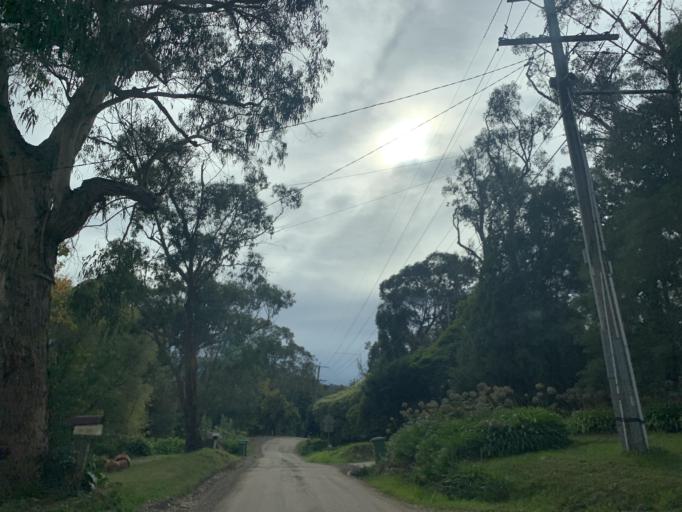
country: AU
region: Victoria
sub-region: Yarra Ranges
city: Belgrave Heights
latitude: -37.9227
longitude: 145.3414
